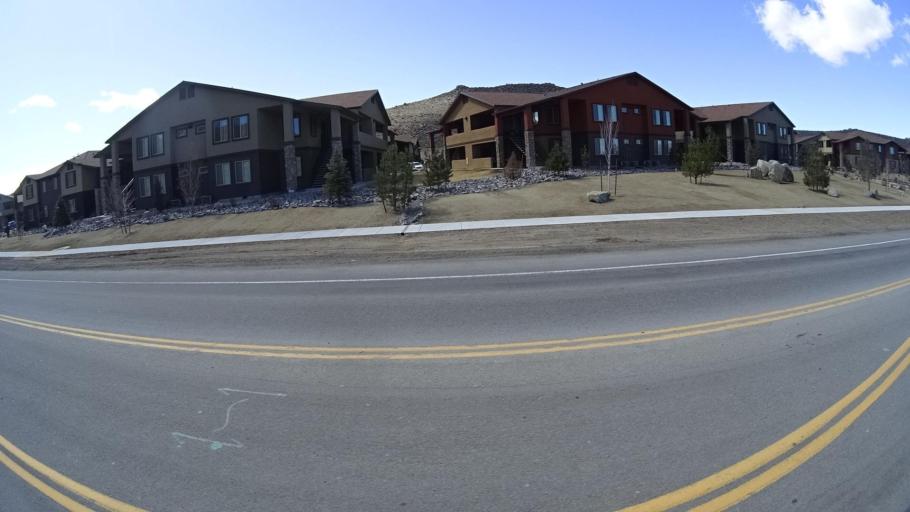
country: US
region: Nevada
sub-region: Washoe County
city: Lemmon Valley
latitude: 39.6252
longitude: -119.8500
